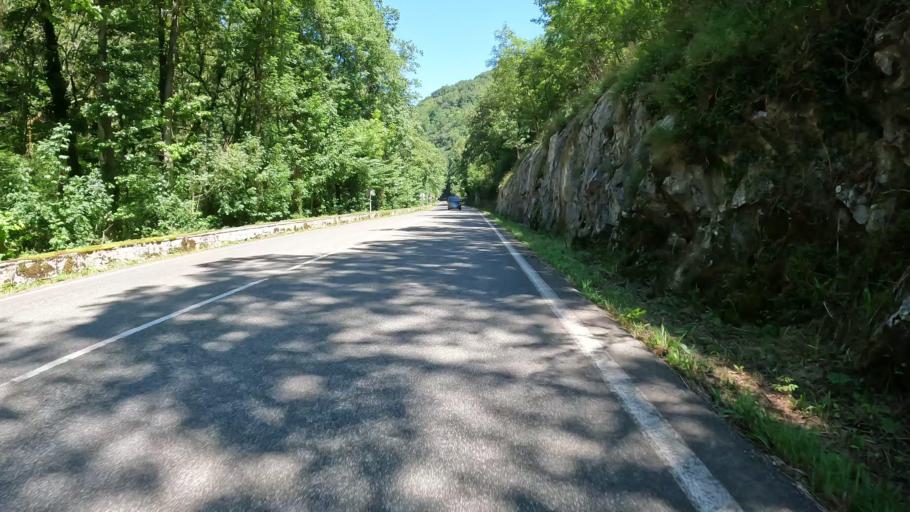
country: ES
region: Basque Country
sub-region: Provincia de Guipuzcoa
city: Oreja
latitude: 43.0714
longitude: -2.0115
